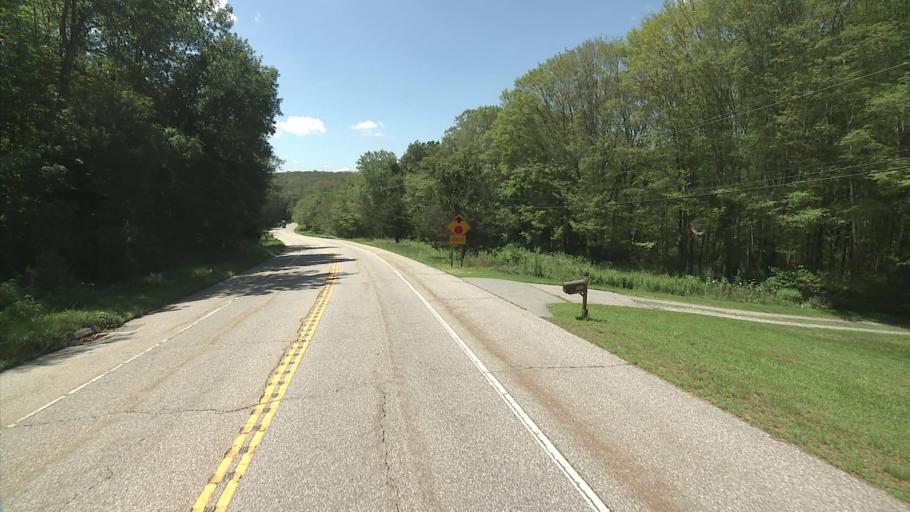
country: US
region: Connecticut
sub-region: Windham County
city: Plainfield Village
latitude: 41.7011
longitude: -71.9594
